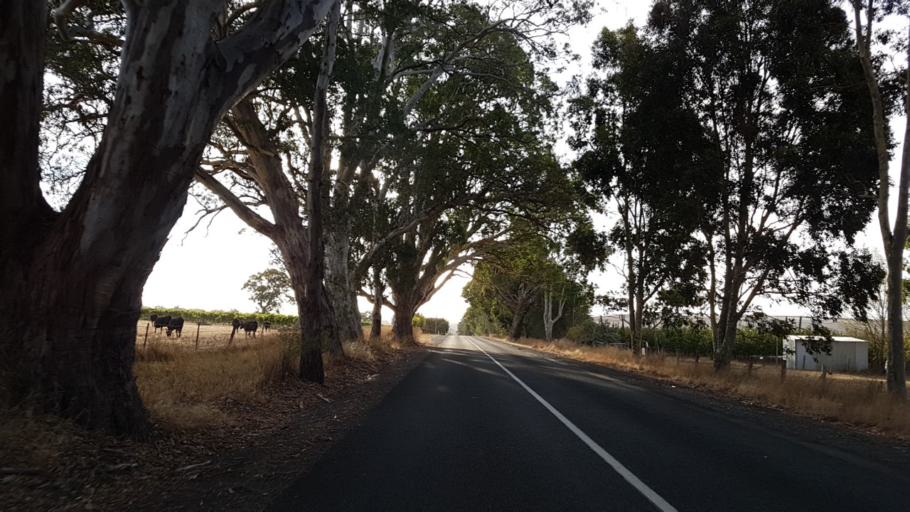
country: AU
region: South Australia
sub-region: Adelaide Hills
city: Woodside
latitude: -34.9784
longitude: 138.8812
